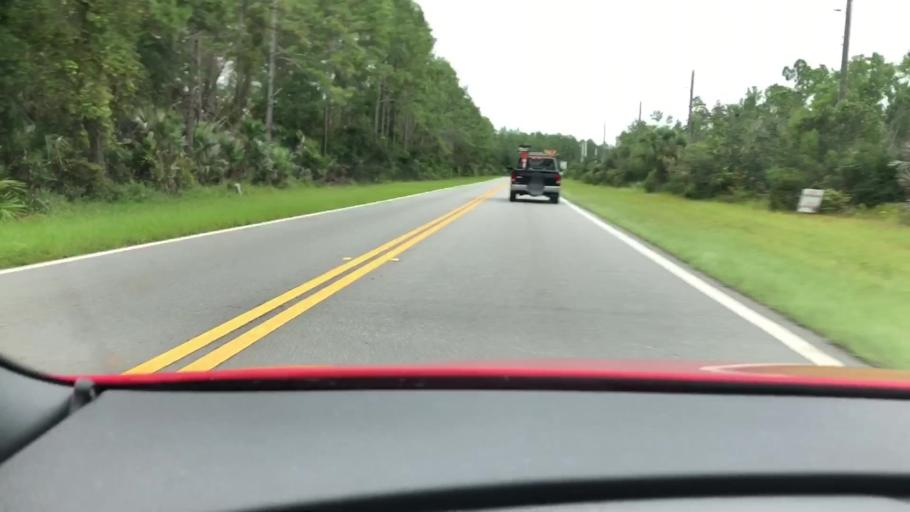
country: US
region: Florida
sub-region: Flagler County
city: Palm Coast
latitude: 29.5352
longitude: -81.2038
